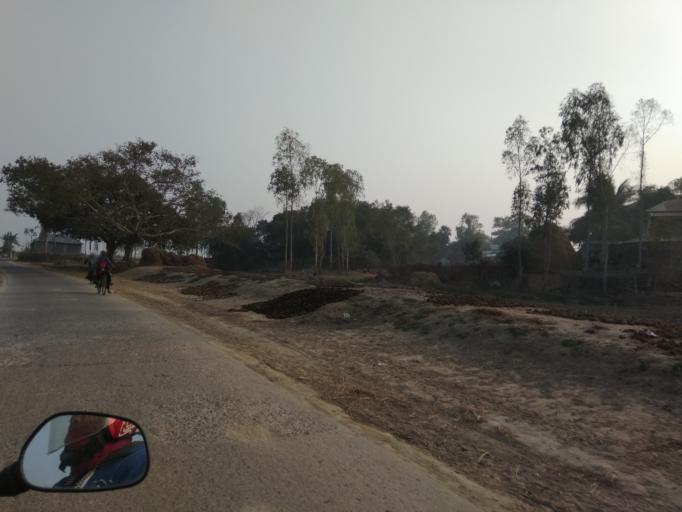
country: BD
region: Rajshahi
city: Ishurdi
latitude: 24.4908
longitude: 89.2027
